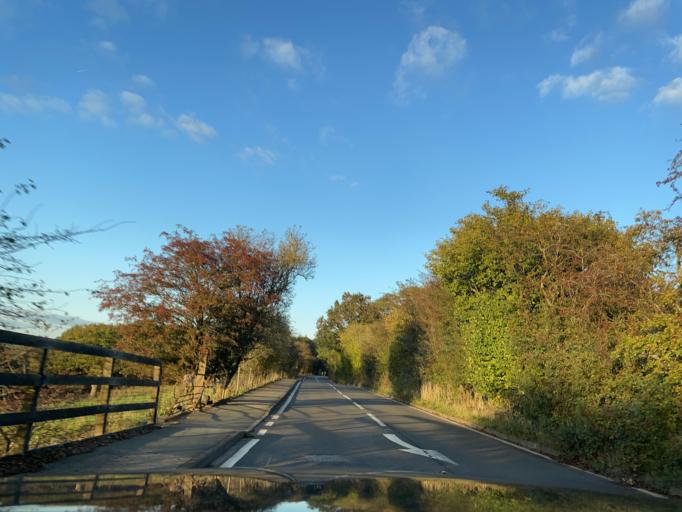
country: GB
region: England
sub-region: Borough of Stockport
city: Marple
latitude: 53.4157
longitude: -2.0334
